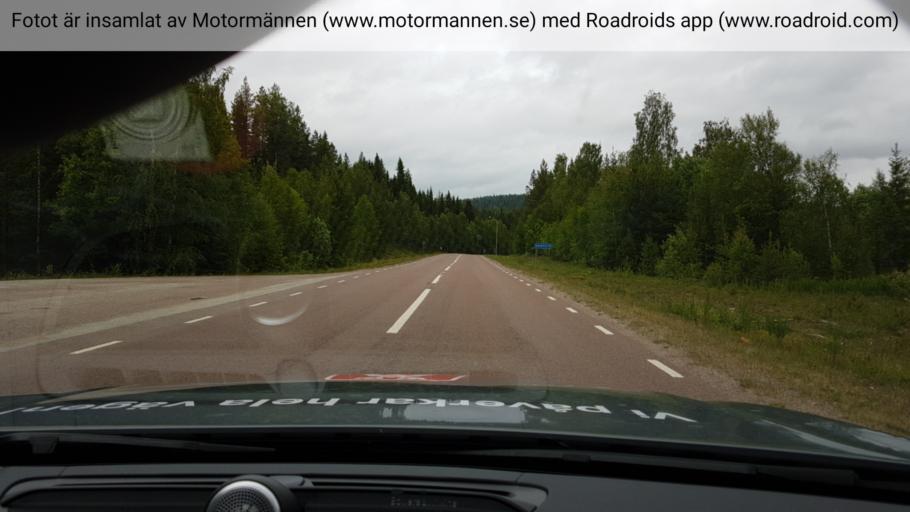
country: SE
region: Jaemtland
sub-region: Braecke Kommun
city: Braecke
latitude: 62.9573
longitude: 15.7481
